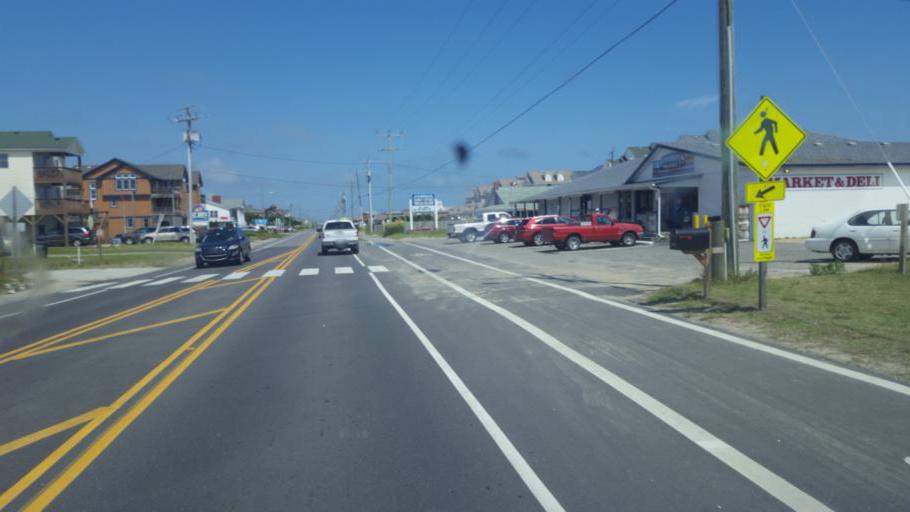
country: US
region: North Carolina
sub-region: Dare County
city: Nags Head
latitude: 35.9098
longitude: -75.5974
